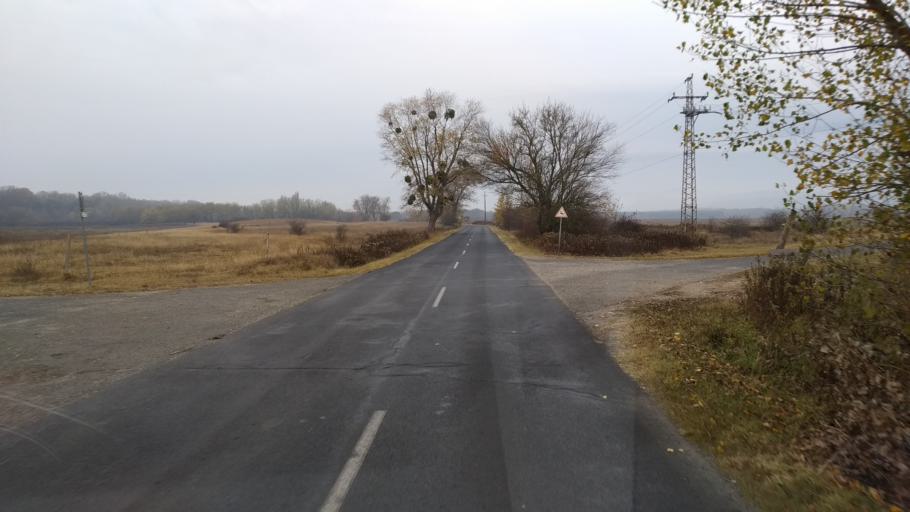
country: HU
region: Pest
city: Tahitotfalu
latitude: 47.7879
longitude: 19.0883
